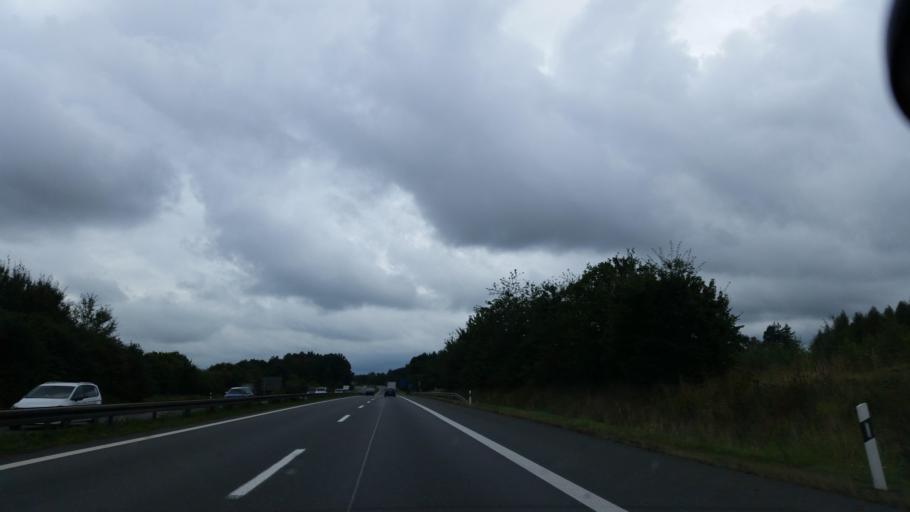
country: DE
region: Saxony
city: Waldkirchen
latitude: 50.5980
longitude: 12.3553
